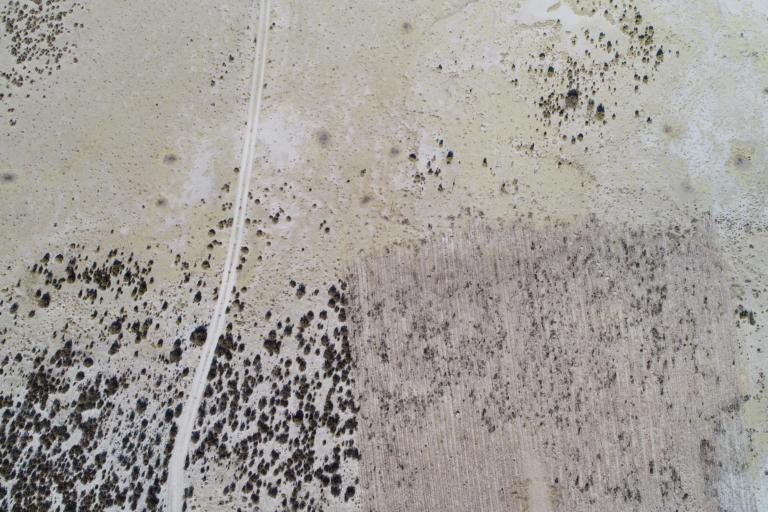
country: BO
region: Potosi
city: Colchani
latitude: -20.3497
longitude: -66.8851
